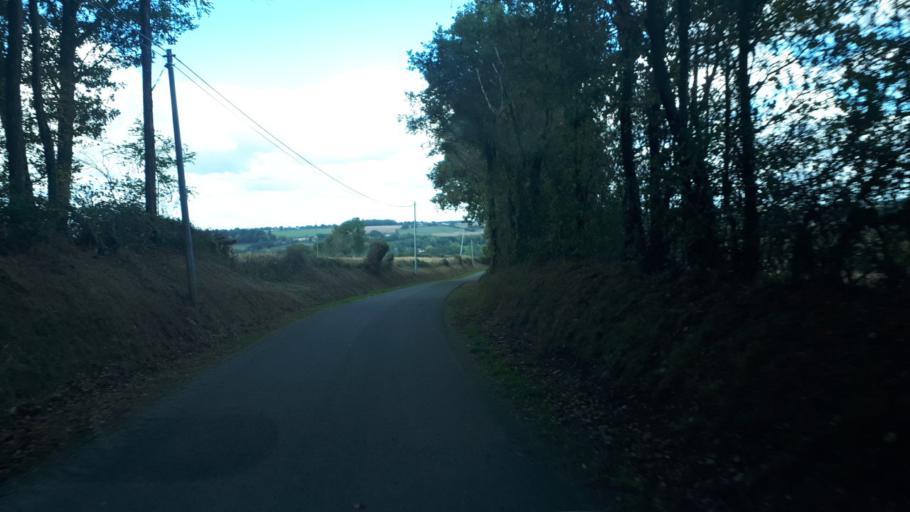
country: FR
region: Centre
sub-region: Departement du Loir-et-Cher
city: Sarge-sur-Braye
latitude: 47.9130
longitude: 0.8606
